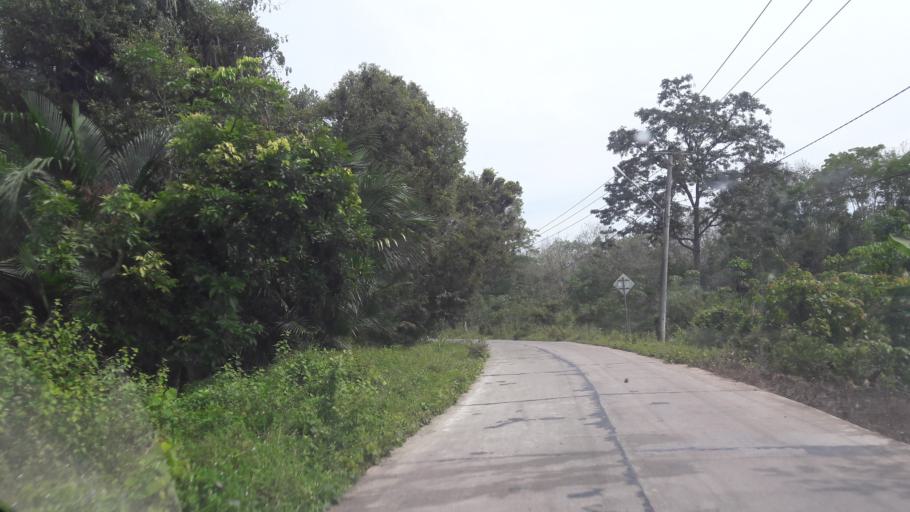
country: ID
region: South Sumatra
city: Gunungmenang
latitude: -3.2280
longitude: 104.1126
